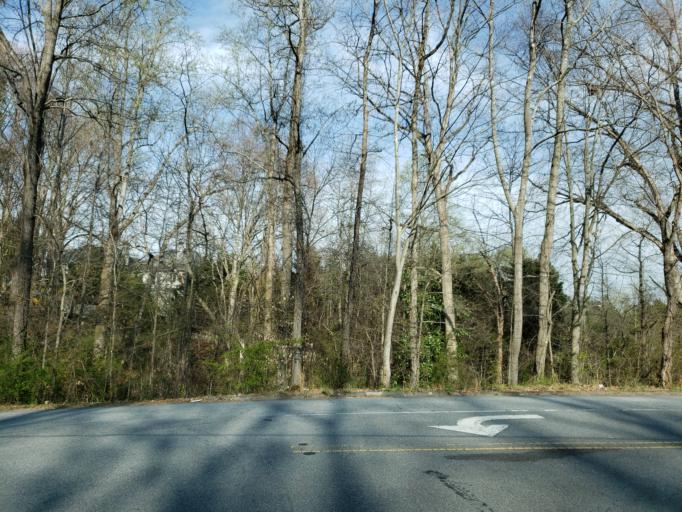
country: US
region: Georgia
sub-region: Cobb County
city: Marietta
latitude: 33.9771
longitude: -84.4694
